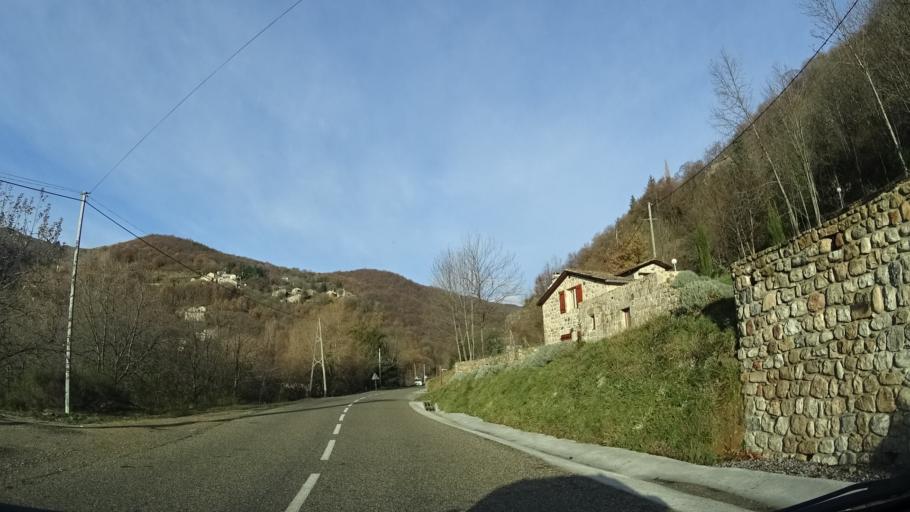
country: FR
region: Rhone-Alpes
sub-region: Departement de l'Ardeche
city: Thueyts
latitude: 44.7281
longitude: 4.2586
